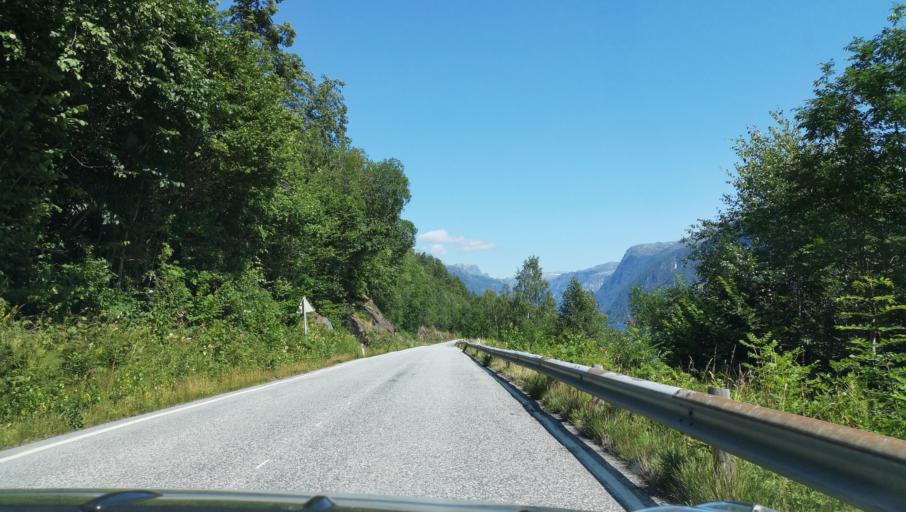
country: NO
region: Hordaland
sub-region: Ulvik
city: Ulvik
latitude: 60.5001
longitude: 6.8981
